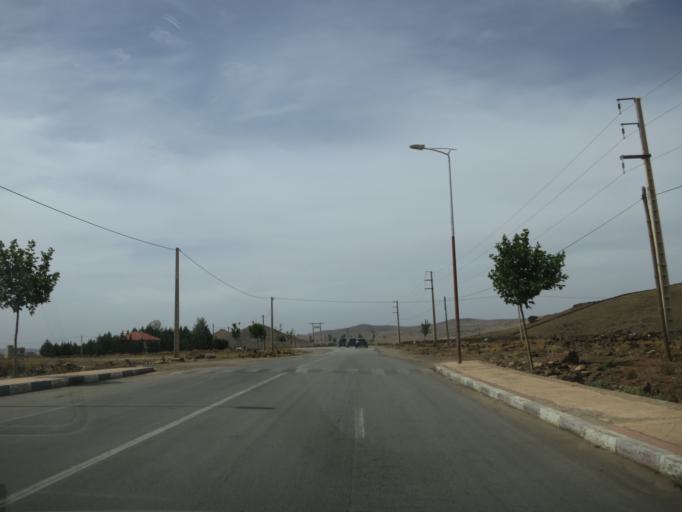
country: MA
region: Meknes-Tafilalet
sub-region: Ifrane
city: Azrou
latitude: 33.2307
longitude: -5.0590
